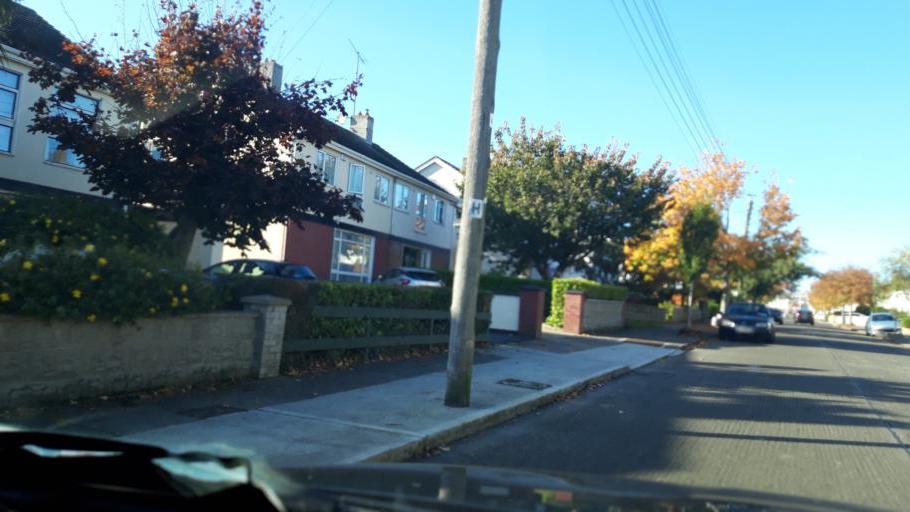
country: IE
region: Leinster
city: Raheny
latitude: 53.3862
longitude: -6.1712
